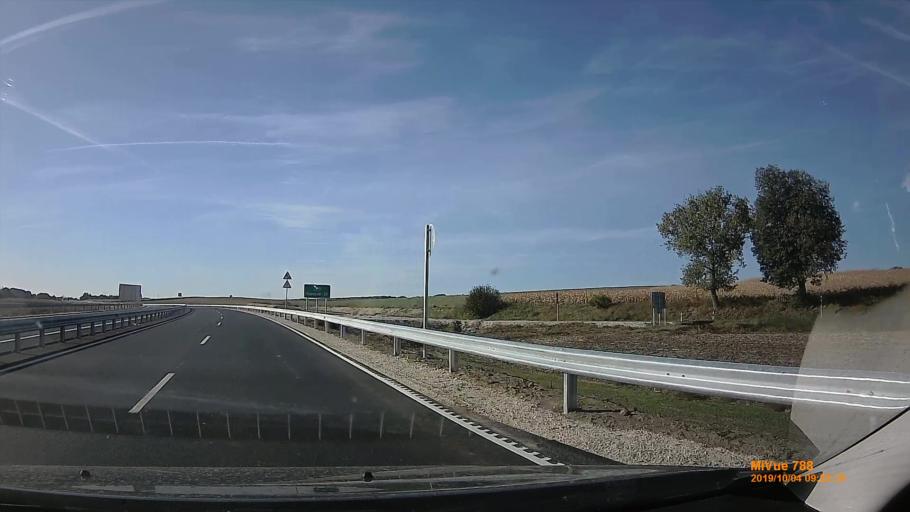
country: HU
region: Somogy
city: Karad
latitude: 46.5496
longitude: 17.8139
